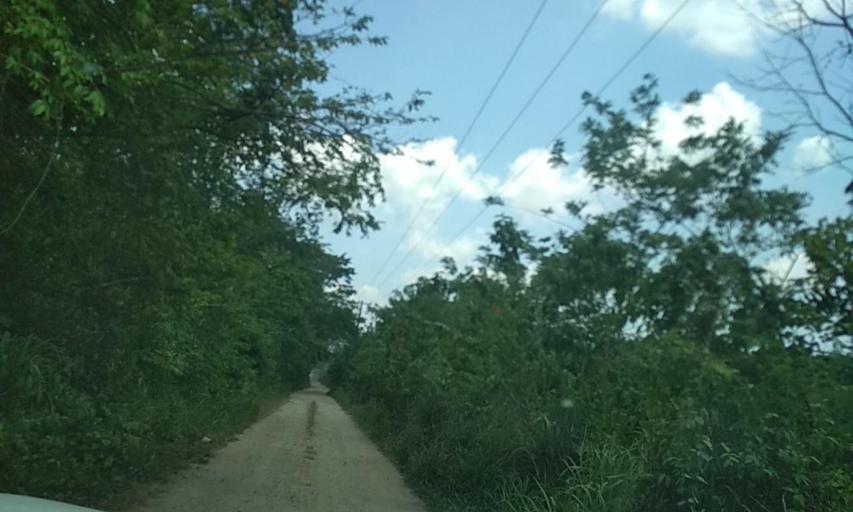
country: MX
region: Chiapas
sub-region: Tecpatan
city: Raudales Malpaso
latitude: 17.2864
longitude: -93.8394
